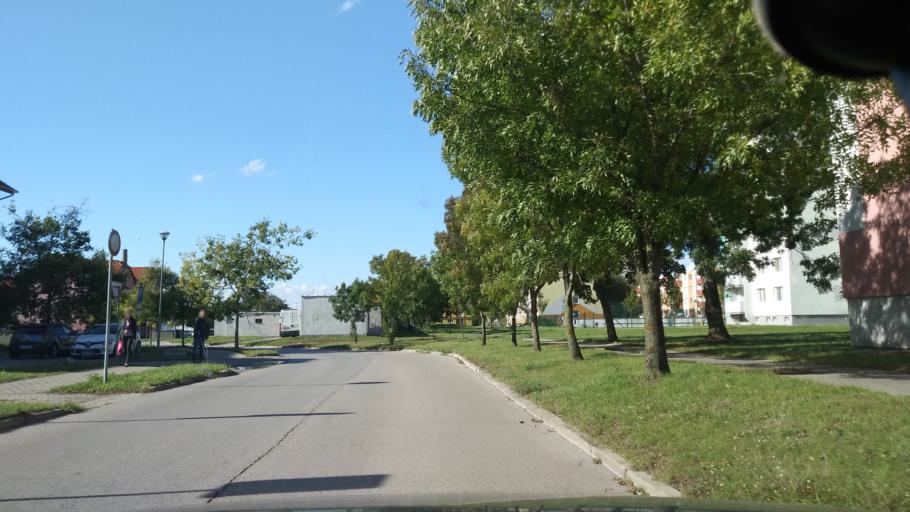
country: SK
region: Trnavsky
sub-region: Okres Skalica
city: Skalica
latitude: 48.8383
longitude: 17.2226
